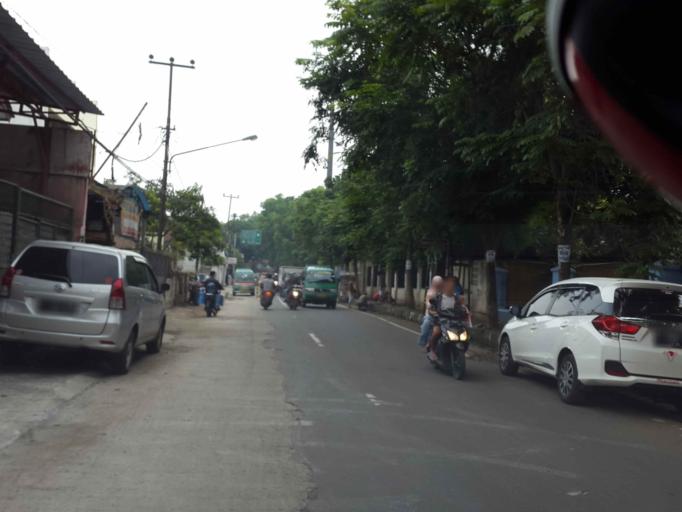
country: ID
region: West Java
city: Margahayukencana
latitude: -6.9248
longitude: 107.5637
